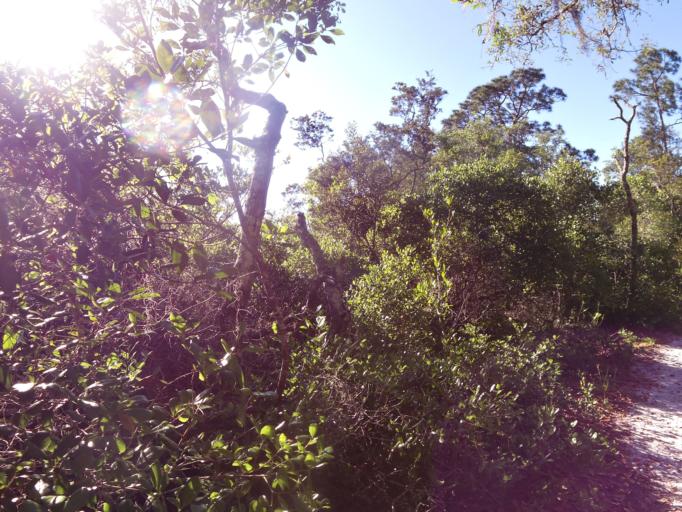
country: US
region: Florida
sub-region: Duval County
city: Atlantic Beach
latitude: 30.3825
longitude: -81.4863
